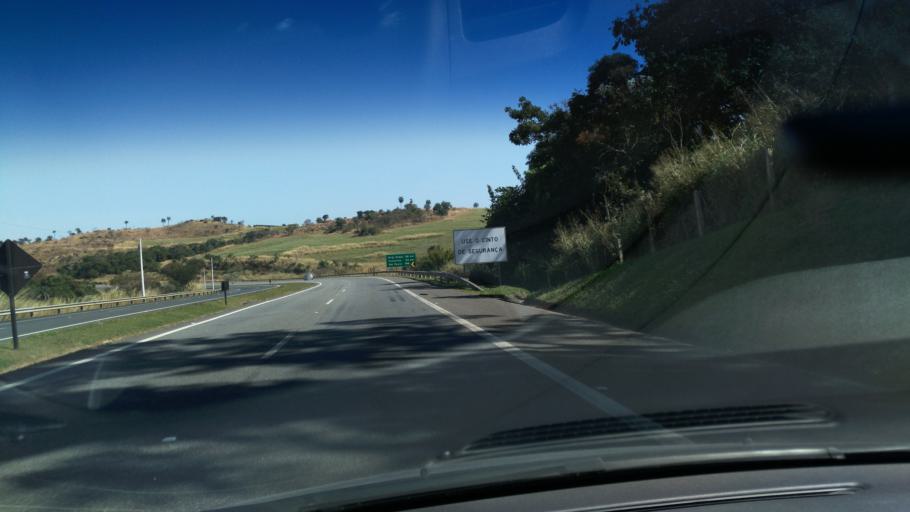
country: BR
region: Sao Paulo
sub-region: Santo Antonio Do Jardim
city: Espirito Santo do Pinhal
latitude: -22.2092
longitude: -46.7817
